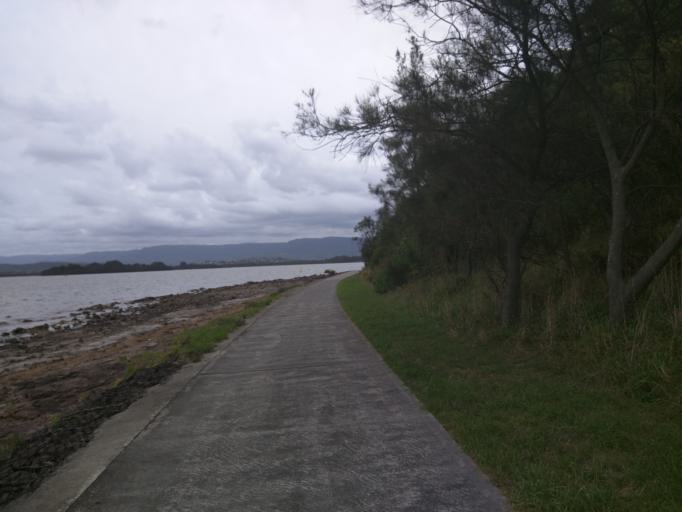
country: AU
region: New South Wales
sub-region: Wollongong
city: Berkeley
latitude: -34.4882
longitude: 150.8601
